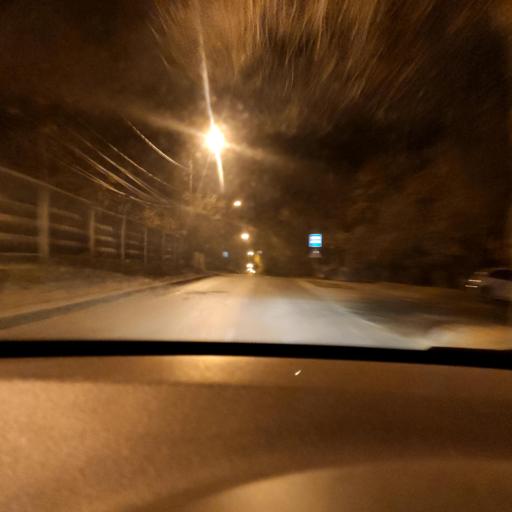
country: RU
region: Samara
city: Samara
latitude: 53.2402
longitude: 50.1783
